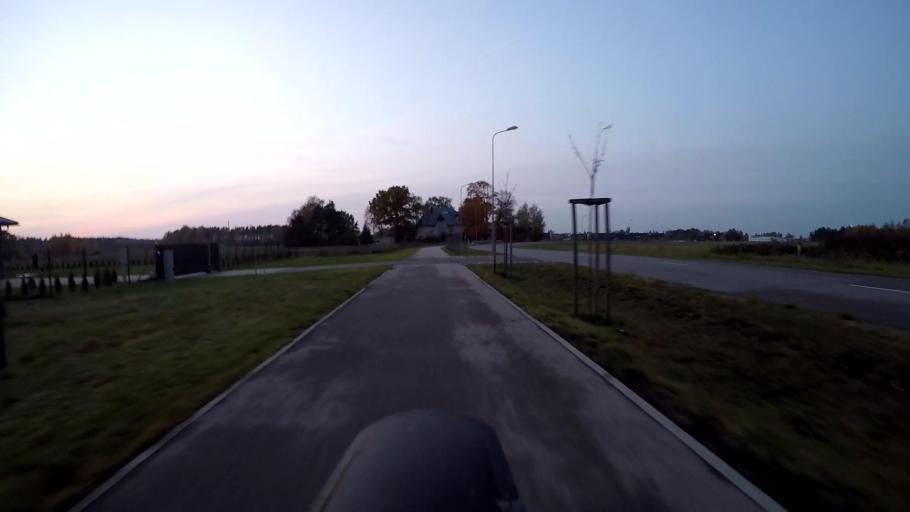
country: LV
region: Marupe
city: Marupe
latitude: 56.9119
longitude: 23.9965
